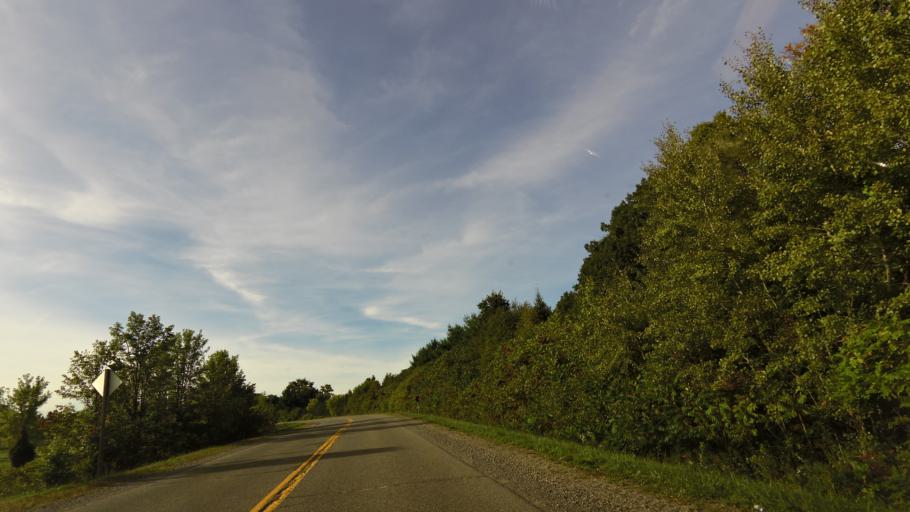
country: CA
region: Ontario
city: Ancaster
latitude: 43.1671
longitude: -79.9522
